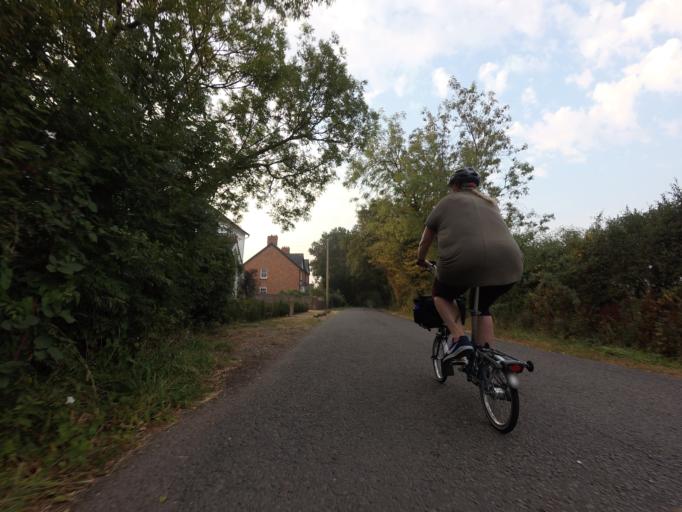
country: GB
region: England
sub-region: Kent
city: Lenham
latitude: 51.1682
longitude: 0.7347
